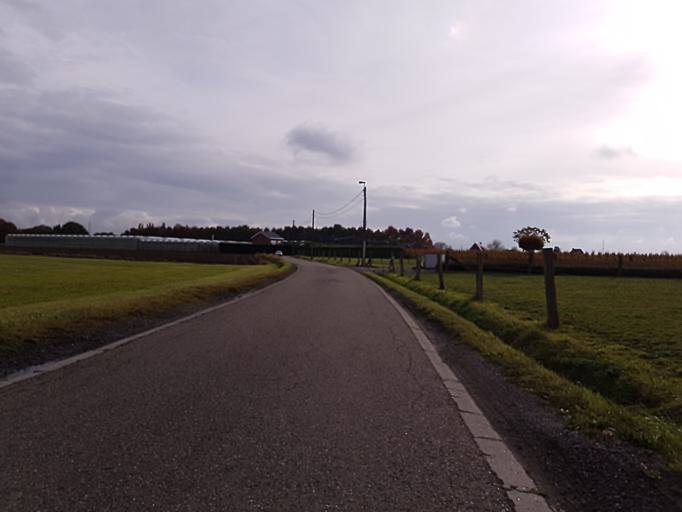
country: BE
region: Flanders
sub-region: Provincie Antwerpen
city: Wommelgem
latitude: 51.1698
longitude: 4.5287
